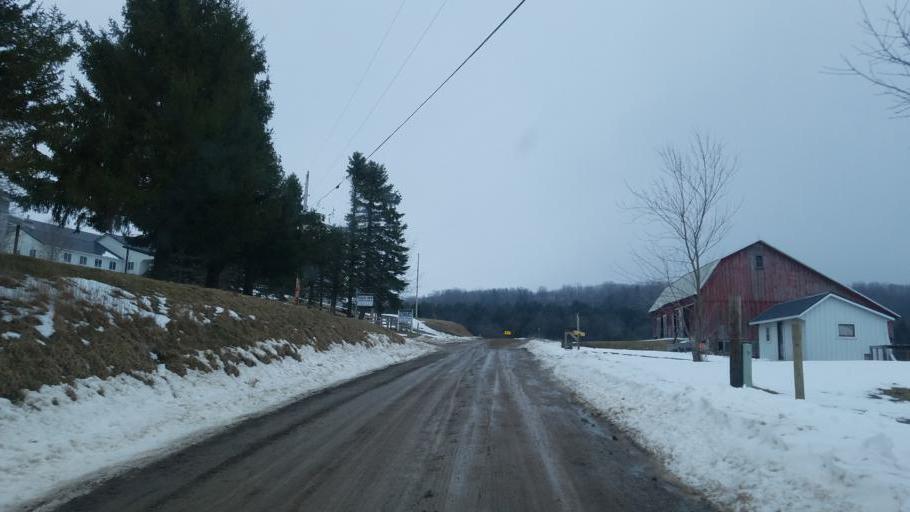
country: US
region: New York
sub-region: Allegany County
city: Andover
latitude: 41.9518
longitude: -77.7766
